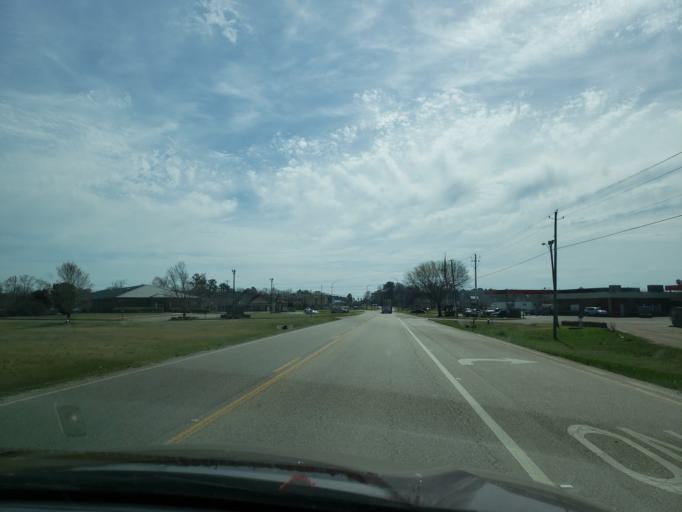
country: US
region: Alabama
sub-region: Dallas County
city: Selma
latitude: 32.4354
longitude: -87.0625
